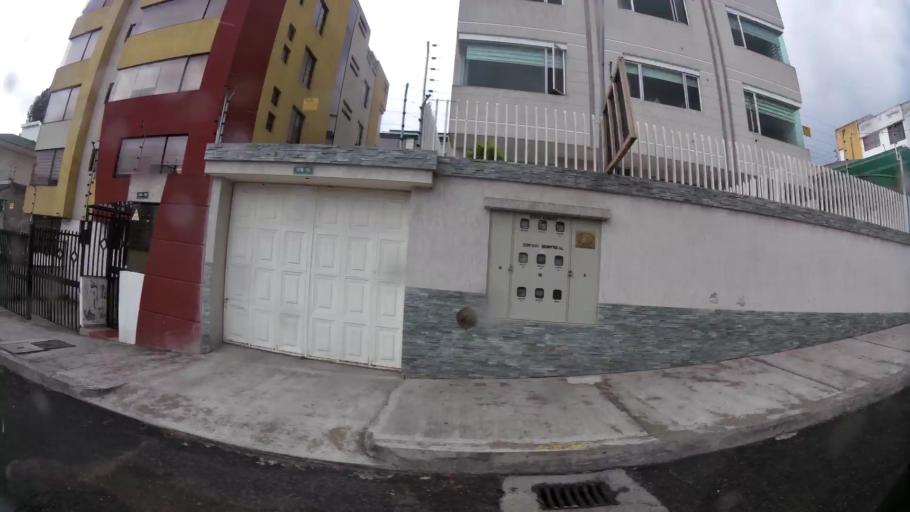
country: EC
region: Pichincha
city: Quito
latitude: -0.0958
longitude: -78.4802
